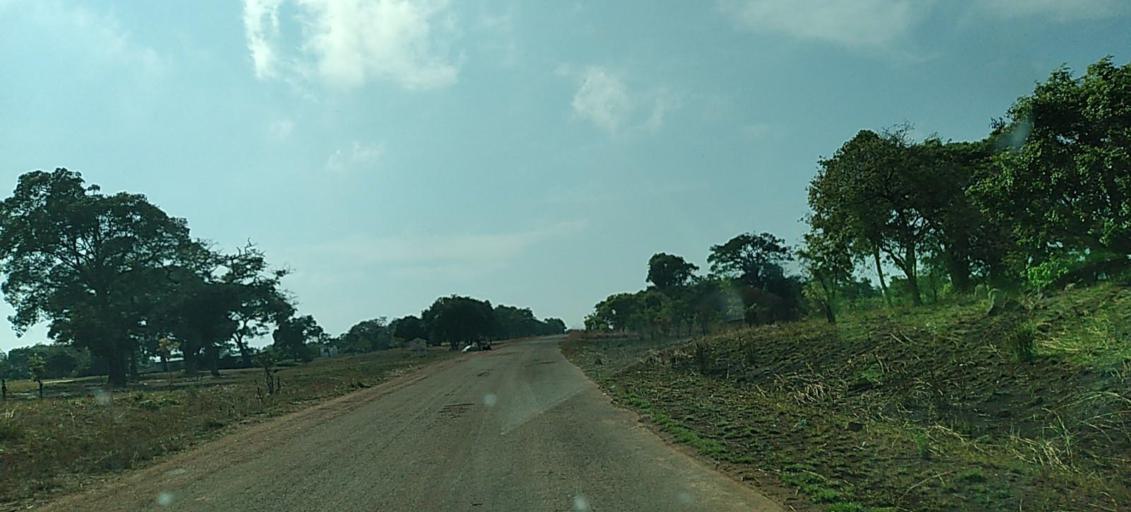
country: ZM
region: North-Western
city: Mwinilunga
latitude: -11.7718
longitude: 25.0121
